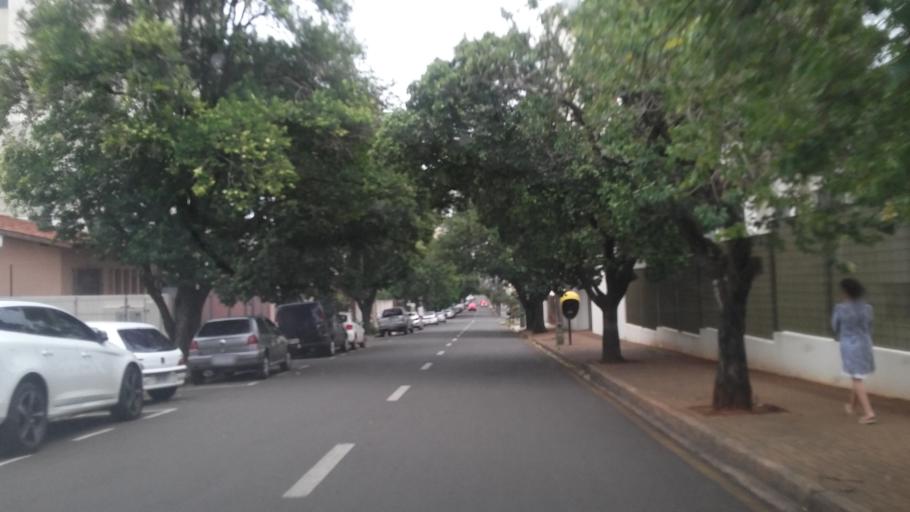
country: BR
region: Parana
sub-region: Londrina
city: Londrina
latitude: -23.3053
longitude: -51.1797
